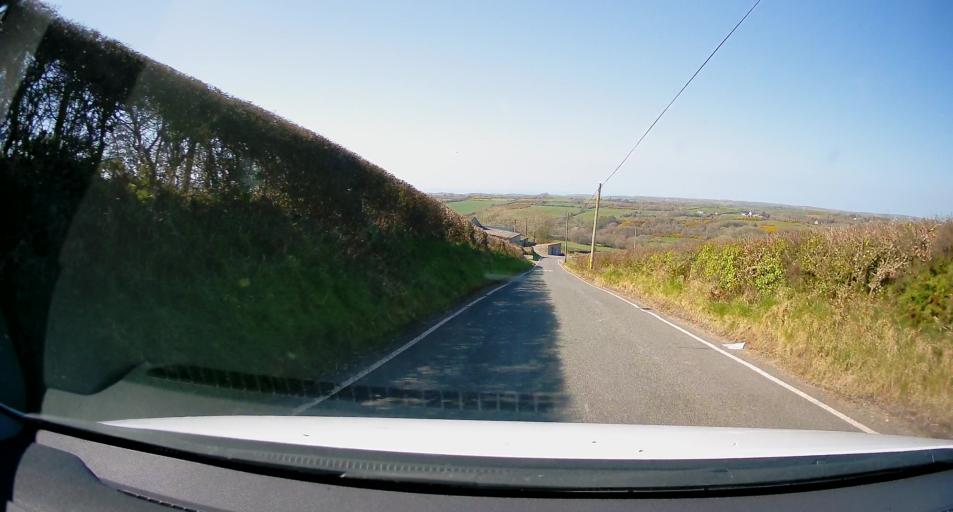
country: GB
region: Wales
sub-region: County of Ceredigion
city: Lledrod
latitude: 52.2999
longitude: -4.0712
